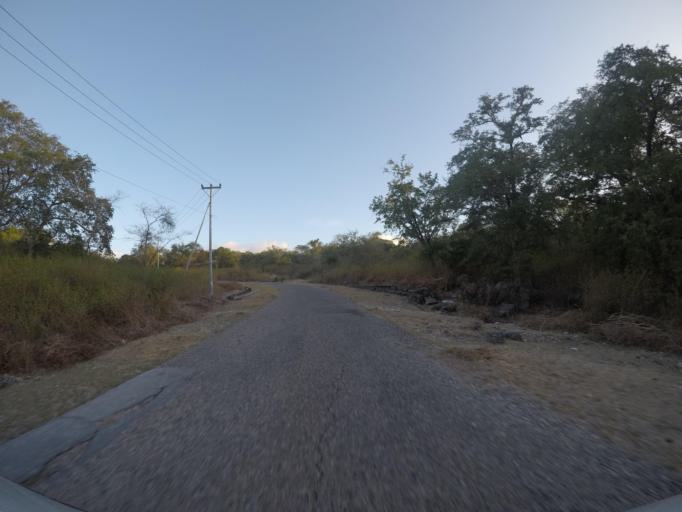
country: TL
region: Lautem
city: Lospalos
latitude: -8.3329
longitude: 127.0055
